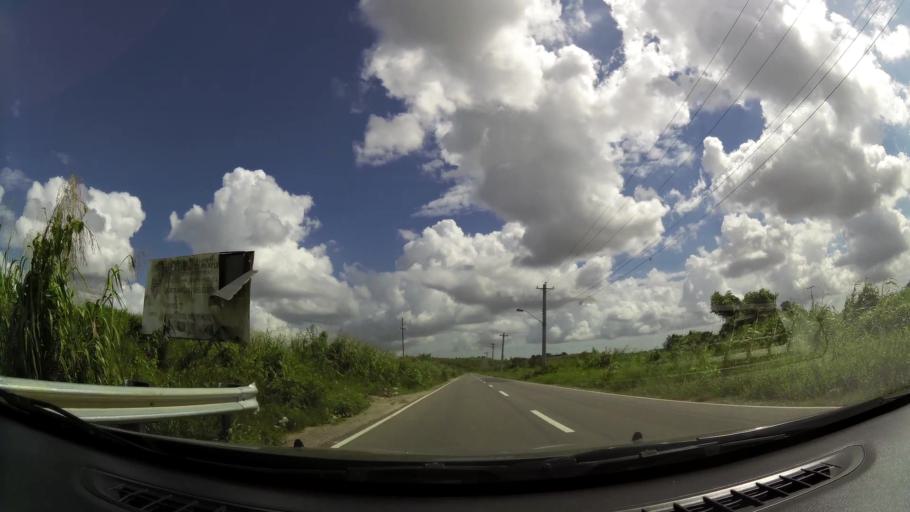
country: TT
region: Penal/Debe
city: Debe
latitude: 10.2331
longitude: -61.4944
